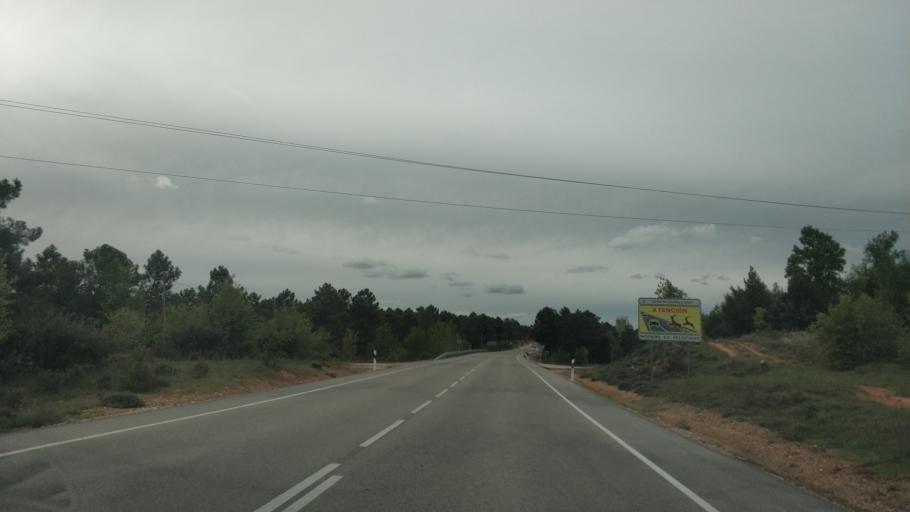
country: ES
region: Castille and Leon
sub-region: Provincia de Soria
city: Quintanas de Gormaz
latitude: 41.5368
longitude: -2.9519
